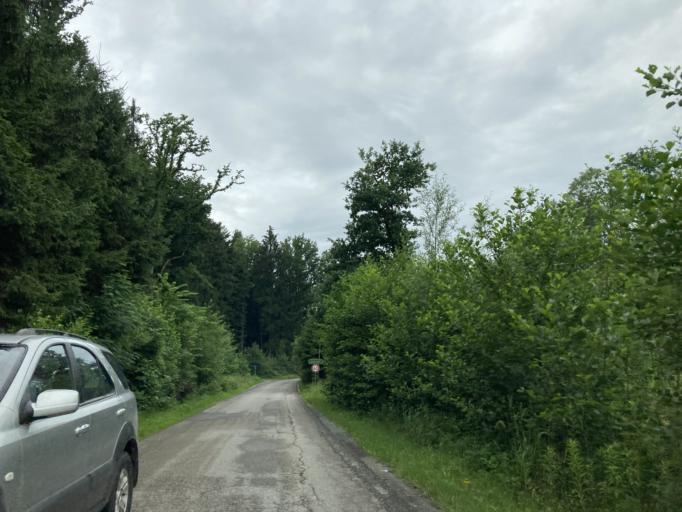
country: DE
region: Bavaria
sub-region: Upper Bavaria
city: Riedering
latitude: 47.8671
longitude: 12.2171
